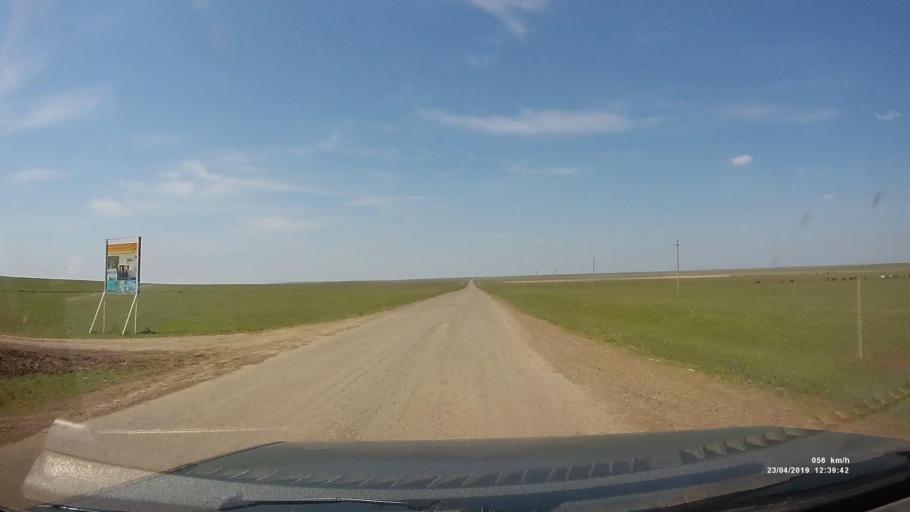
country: RU
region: Kalmykiya
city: Yashalta
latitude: 46.4357
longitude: 42.7057
